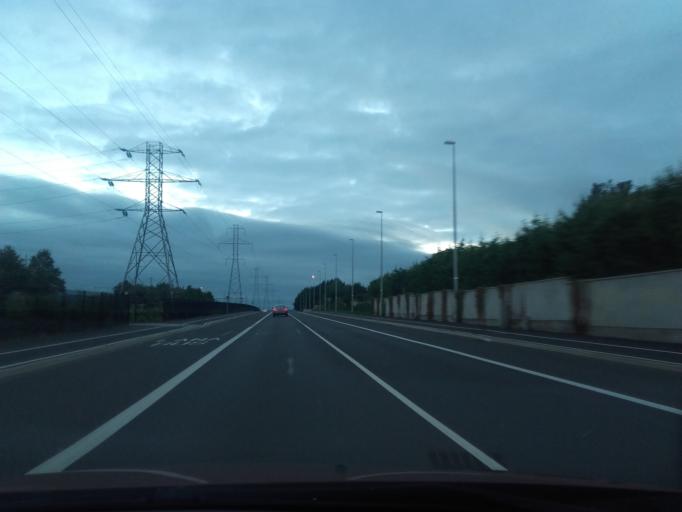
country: IE
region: Leinster
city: Tallaght
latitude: 53.2973
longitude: -6.3803
